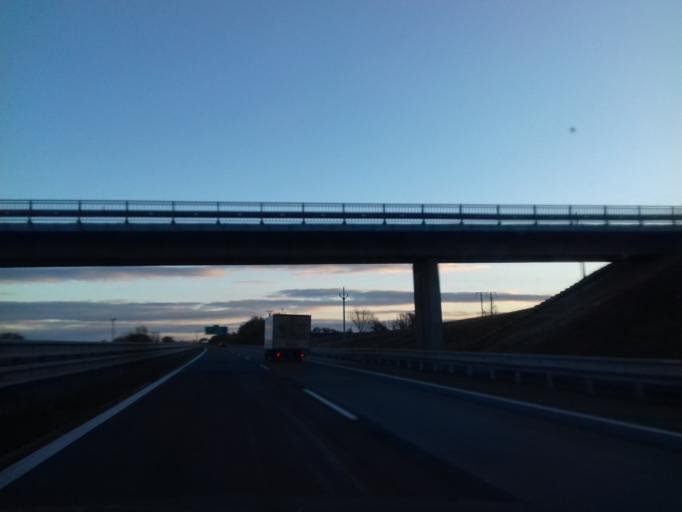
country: CZ
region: South Moravian
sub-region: Okres Vyskov
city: Vyskov
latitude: 49.2614
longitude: 16.9960
